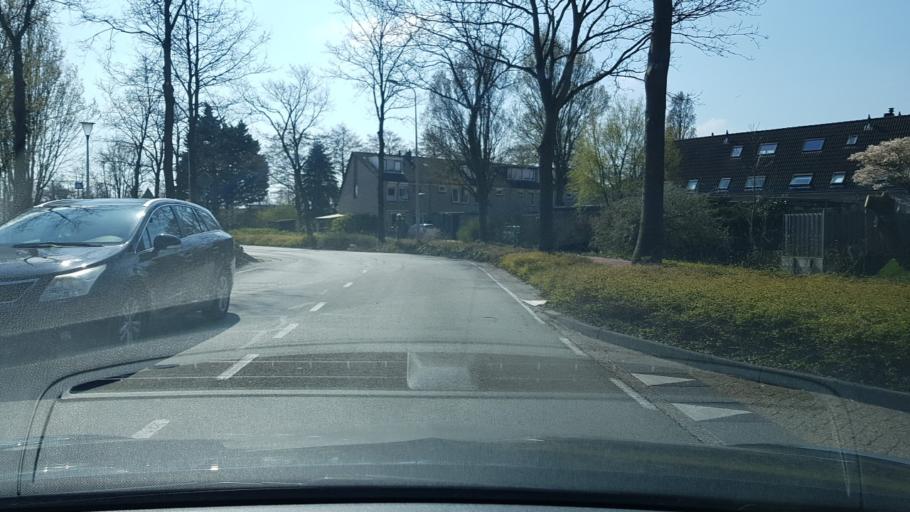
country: NL
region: South Holland
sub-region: Gemeente Teylingen
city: Voorhout
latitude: 52.2223
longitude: 4.4902
